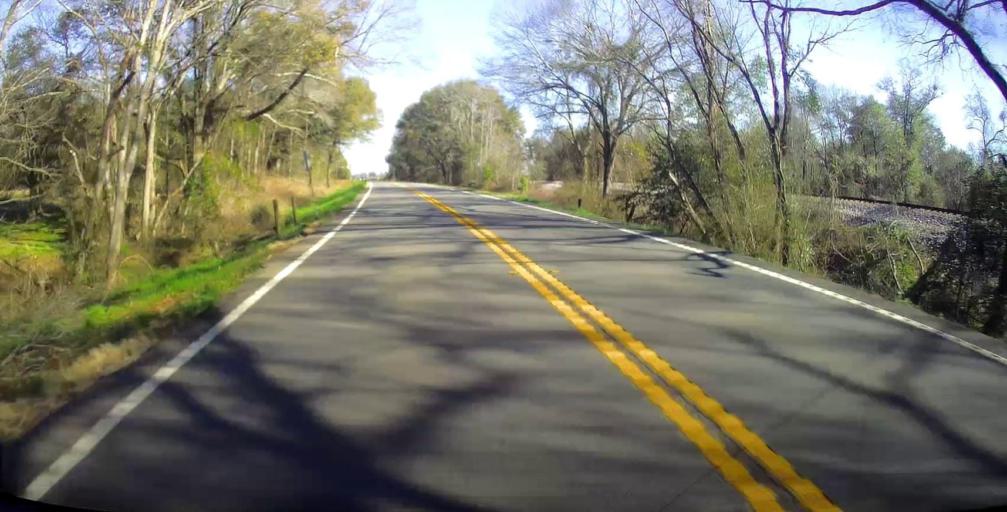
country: US
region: Georgia
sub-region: Macon County
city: Oglethorpe
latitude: 32.3372
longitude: -84.1266
